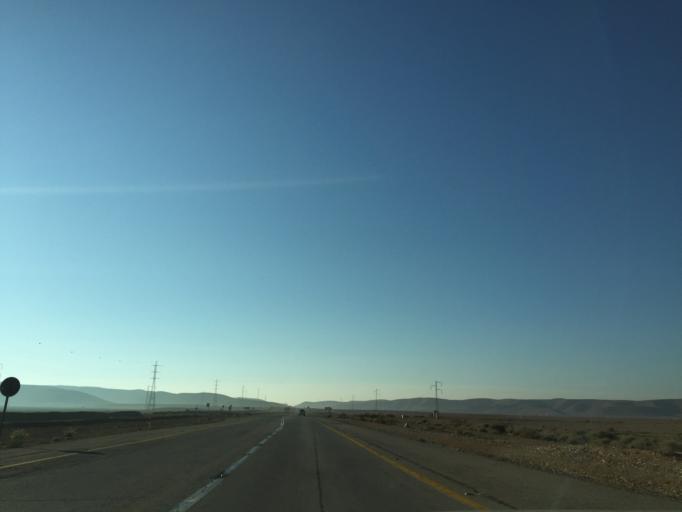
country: IL
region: Southern District
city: Mitzpe Ramon
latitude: 30.4079
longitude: 34.9451
